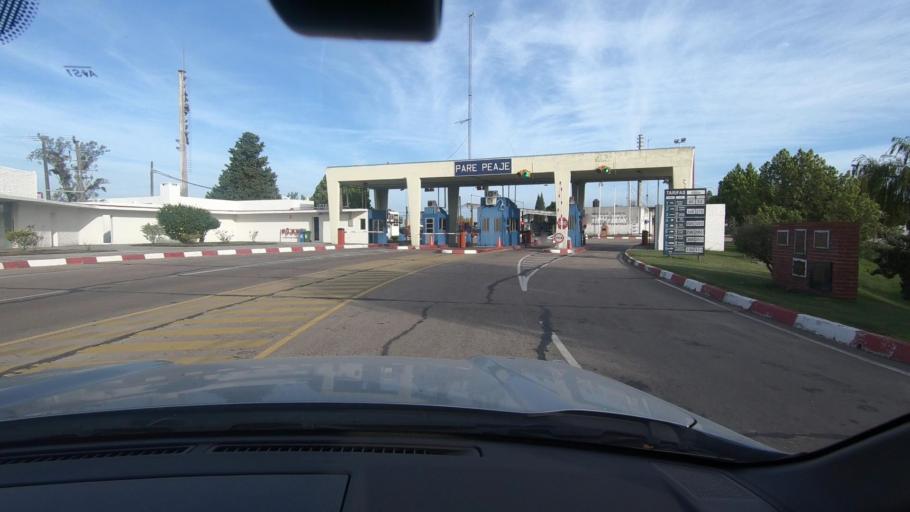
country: AR
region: Entre Rios
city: Colon
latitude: -32.2494
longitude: -58.1429
